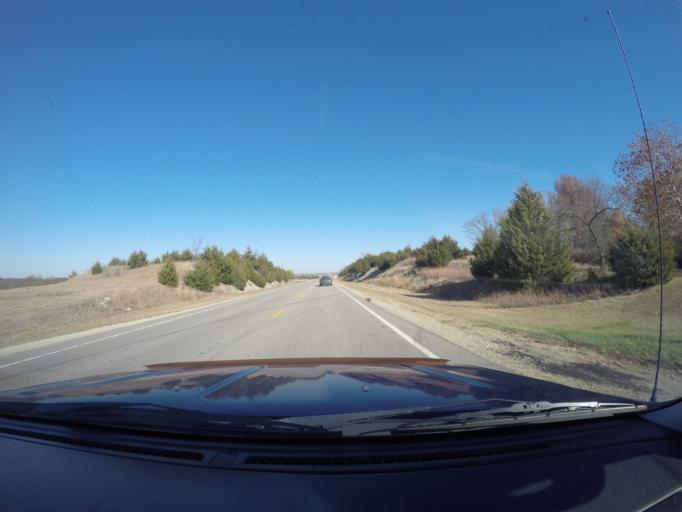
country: US
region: Kansas
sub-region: Marshall County
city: Blue Rapids
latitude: 39.4203
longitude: -96.7644
